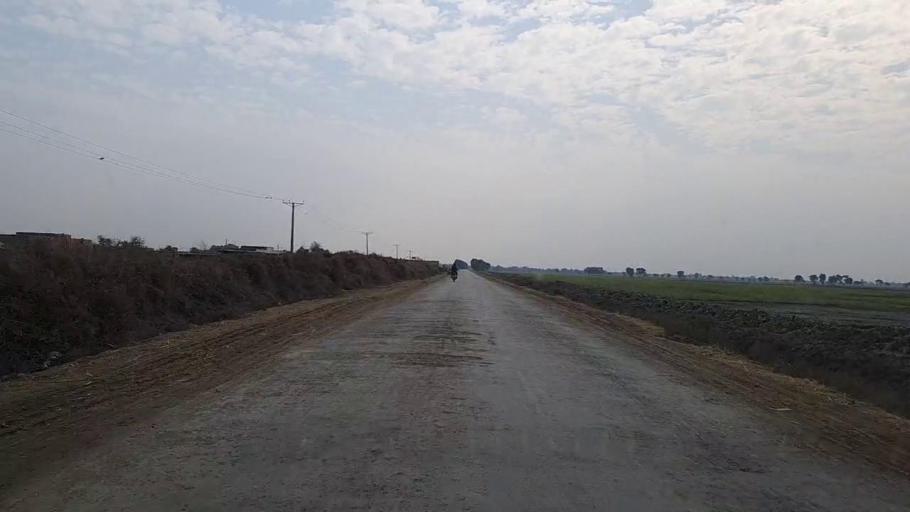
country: PK
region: Sindh
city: Mirwah Gorchani
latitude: 25.3855
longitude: 69.0818
